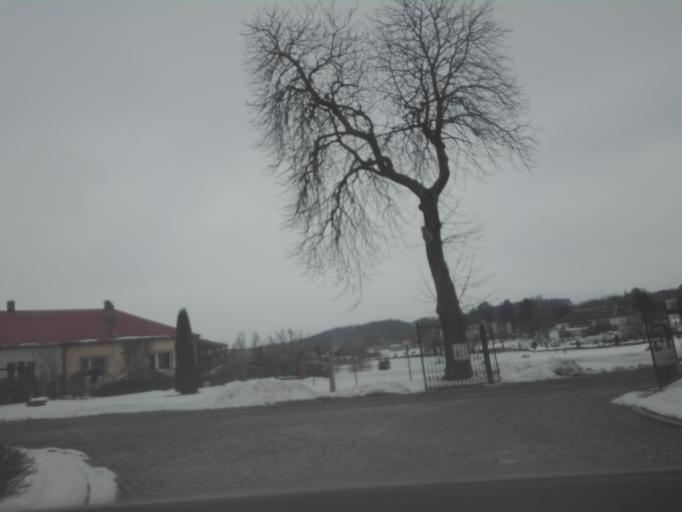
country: PL
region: Lublin Voivodeship
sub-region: Powiat hrubieszowski
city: Horodlo
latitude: 50.8410
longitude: 24.0323
